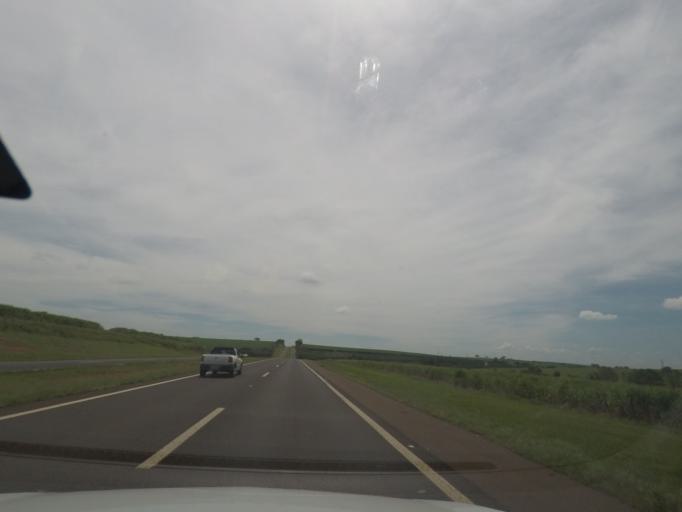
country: BR
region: Sao Paulo
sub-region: Bebedouro
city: Bebedouro
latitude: -21.0339
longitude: -48.4196
